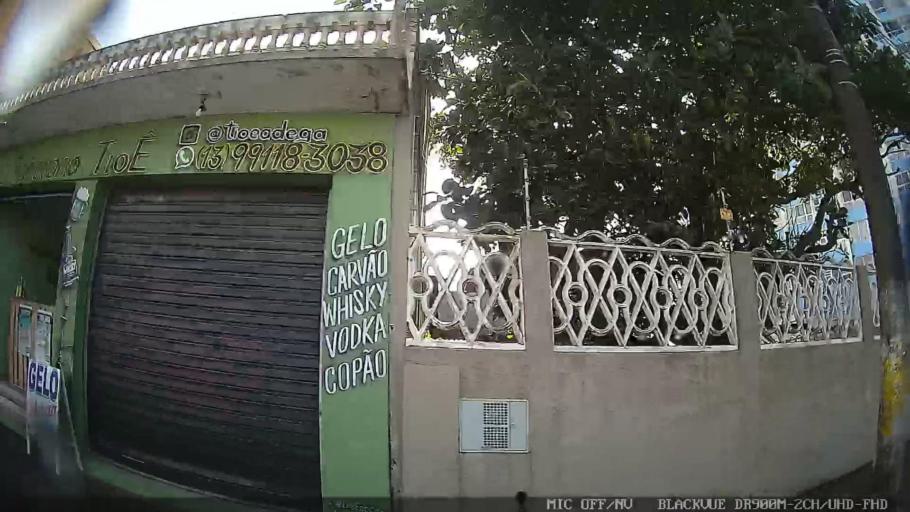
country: BR
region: Sao Paulo
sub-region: Itanhaem
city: Itanhaem
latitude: -24.1862
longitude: -46.8013
